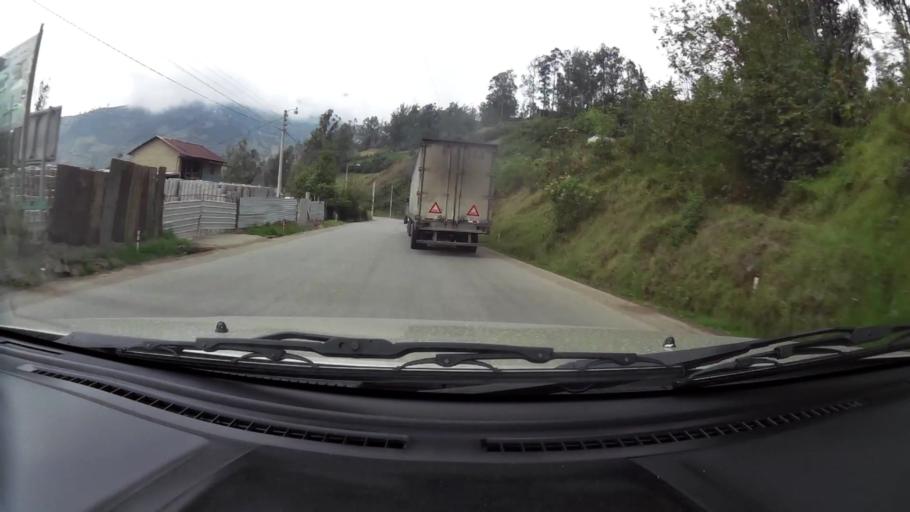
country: EC
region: Chimborazo
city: Alausi
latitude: -2.3076
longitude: -78.9214
